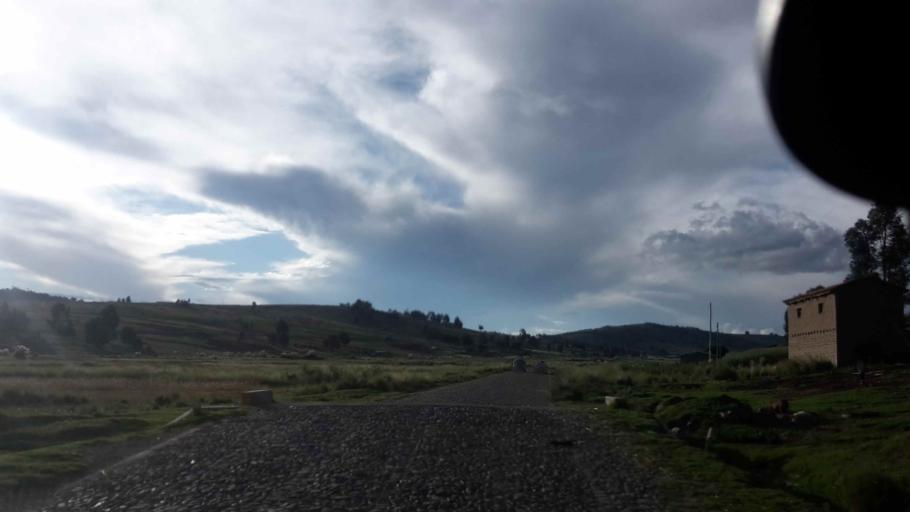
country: BO
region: Cochabamba
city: Arani
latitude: -17.5317
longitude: -65.6571
